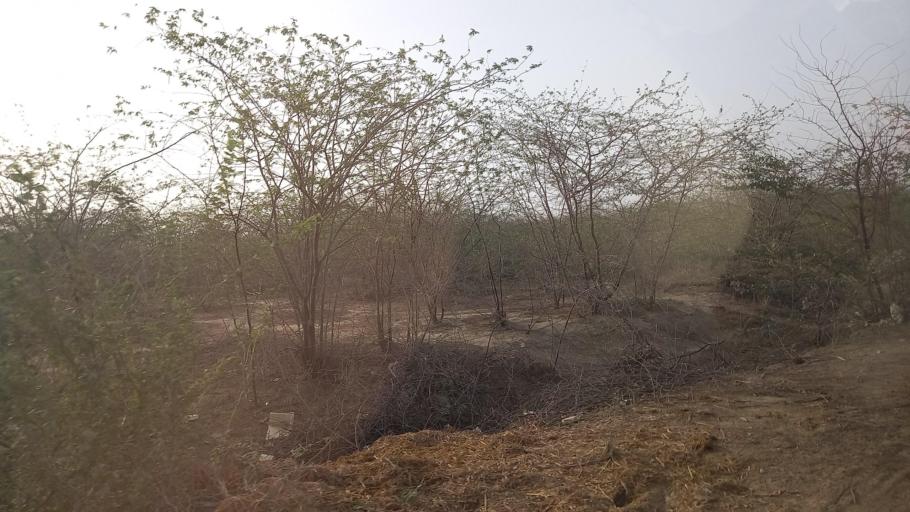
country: PK
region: Sindh
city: Malir Cantonment
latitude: 25.1147
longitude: 67.1915
